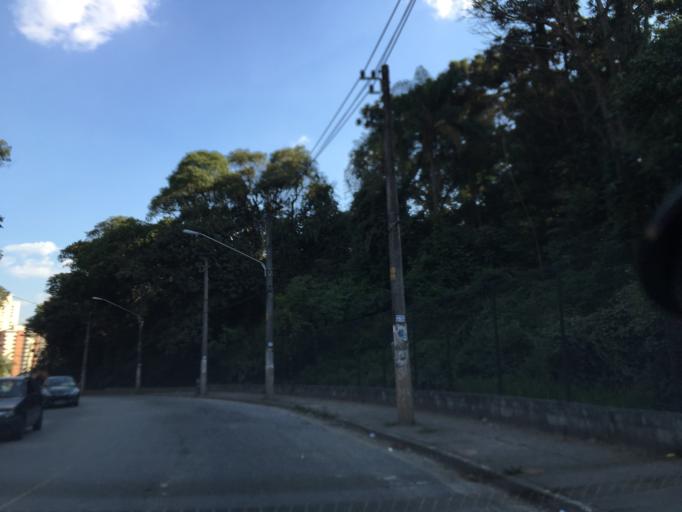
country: BR
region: Sao Paulo
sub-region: Sao Paulo
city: Sao Paulo
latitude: -23.4647
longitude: -46.6297
